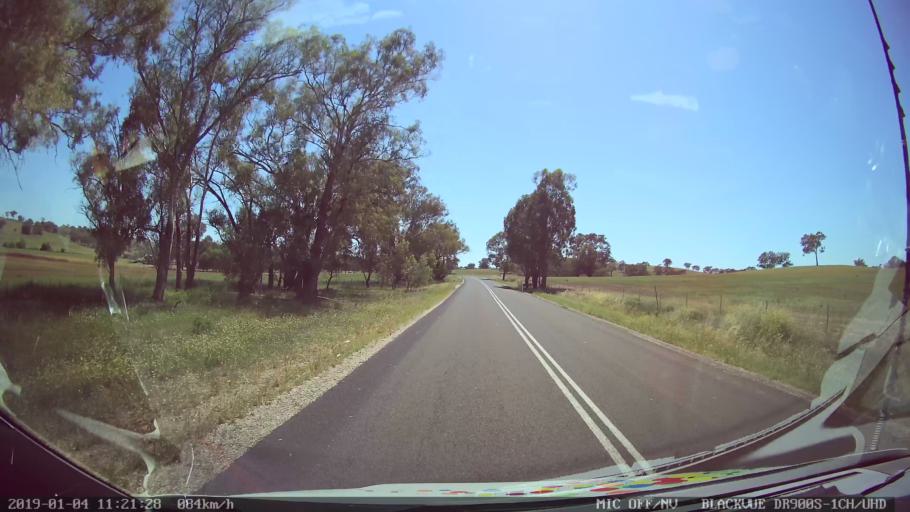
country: AU
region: New South Wales
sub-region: Cabonne
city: Molong
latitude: -33.1543
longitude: 148.7113
